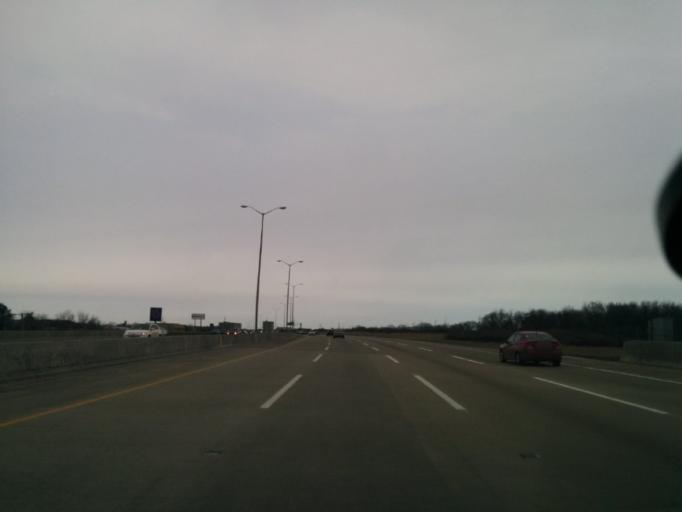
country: US
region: Illinois
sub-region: Cook County
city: Des Plaines
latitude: 42.0826
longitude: -87.8660
